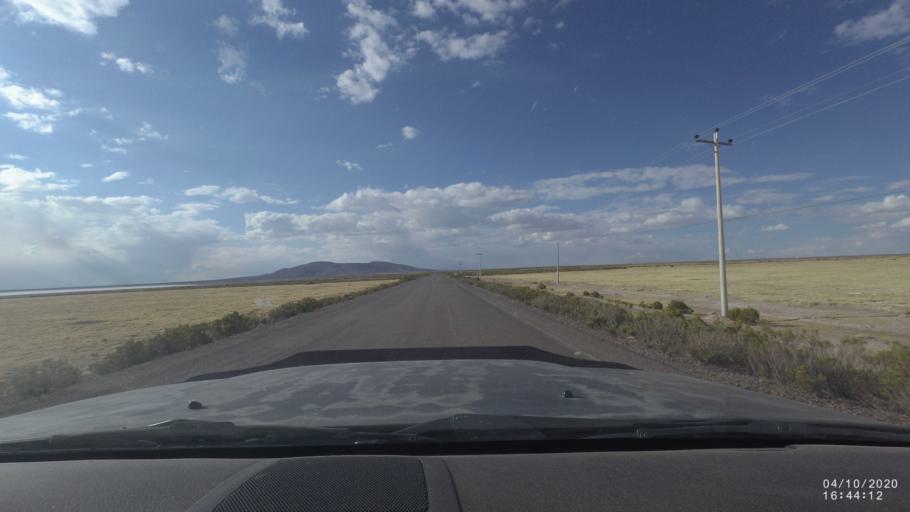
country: BO
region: Oruro
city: Poopo
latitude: -18.6872
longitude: -67.5584
